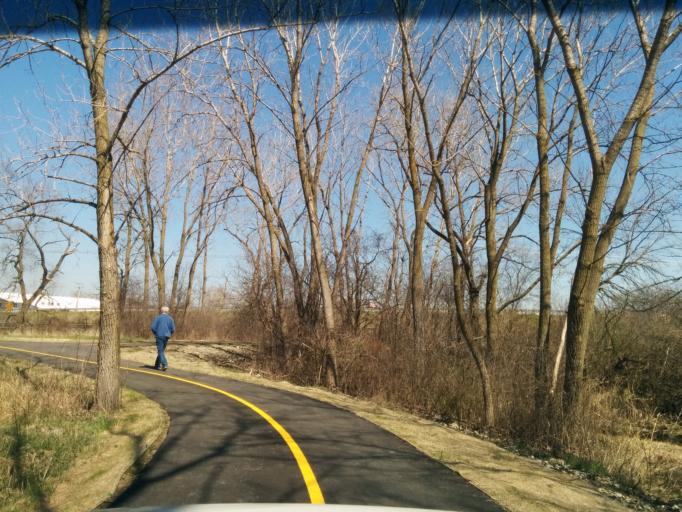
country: US
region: Illinois
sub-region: Cook County
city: Markham
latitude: 41.5988
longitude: -87.7177
